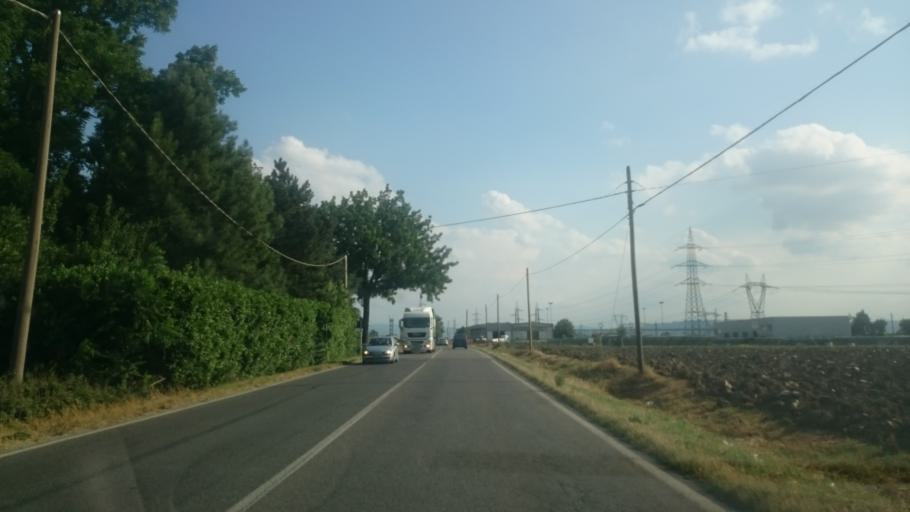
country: IT
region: Emilia-Romagna
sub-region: Provincia di Reggio Emilia
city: Rubiera
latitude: 44.6318
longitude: 10.7778
